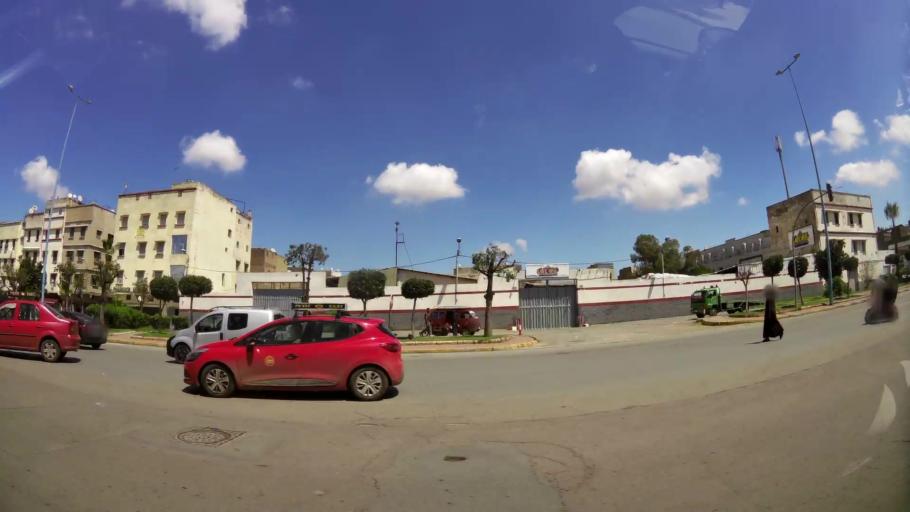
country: MA
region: Grand Casablanca
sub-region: Casablanca
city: Casablanca
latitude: 33.5543
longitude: -7.5921
